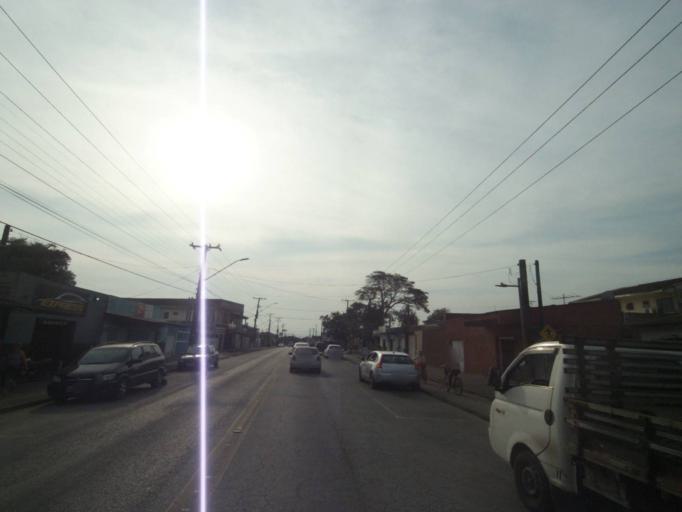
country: BR
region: Parana
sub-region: Paranagua
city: Paranagua
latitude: -25.5178
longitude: -48.5392
